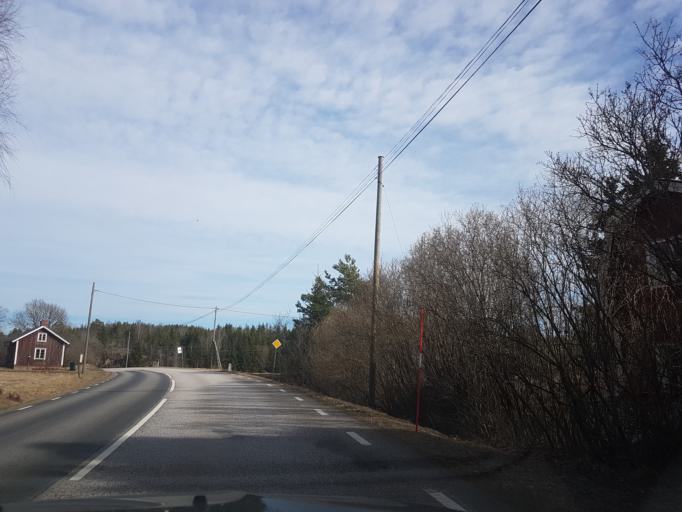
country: SE
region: Stockholm
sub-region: Norrtalje Kommun
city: Rimbo
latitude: 59.7278
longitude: 18.5115
